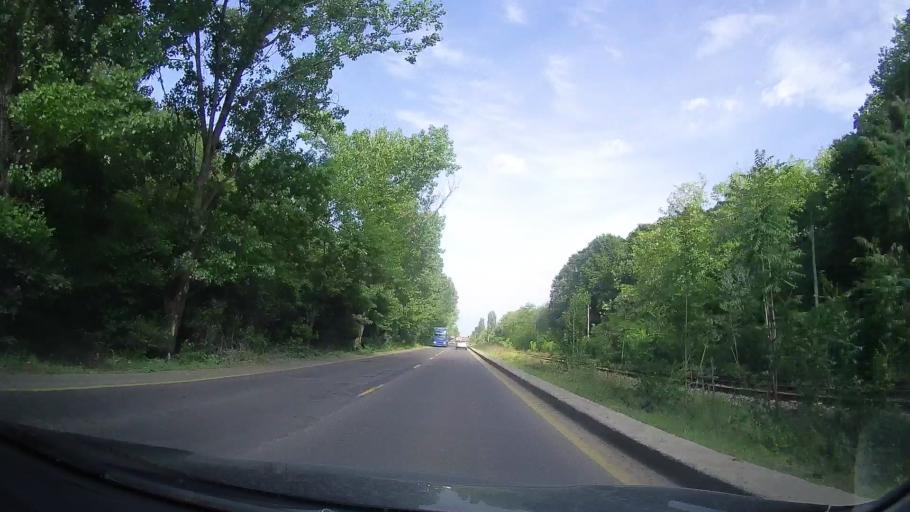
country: RO
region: Ilfov
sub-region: Comuna Magurele
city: Alunisu
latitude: 44.3538
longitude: 26.0532
